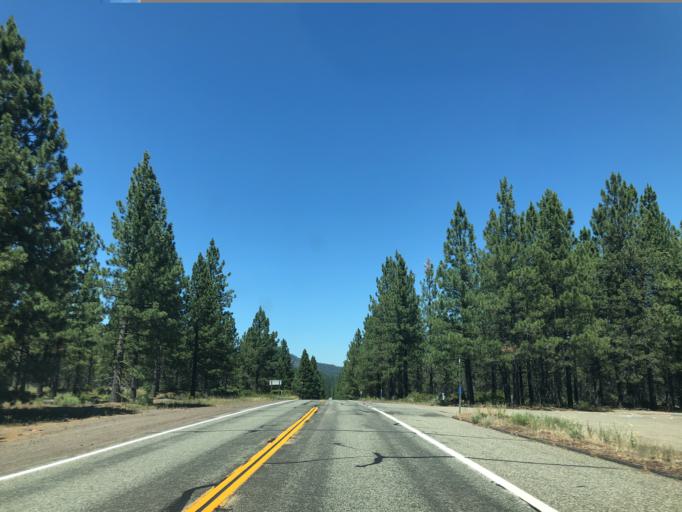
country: US
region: California
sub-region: Shasta County
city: Burney
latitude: 40.6250
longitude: -121.4796
